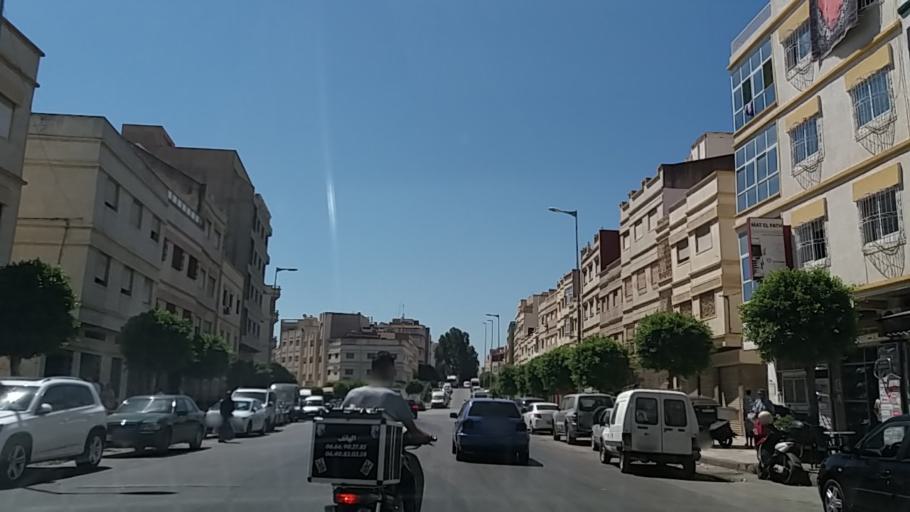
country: MA
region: Tanger-Tetouan
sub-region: Tanger-Assilah
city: Tangier
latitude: 35.7569
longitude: -5.8014
